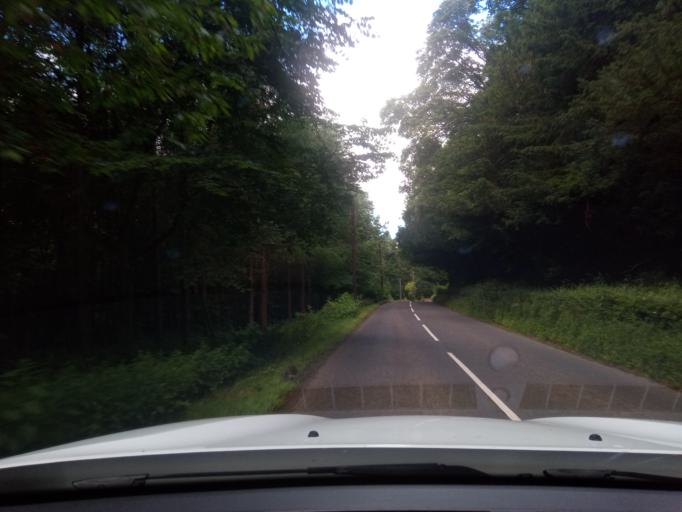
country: GB
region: Scotland
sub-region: The Scottish Borders
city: Selkirk
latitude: 55.5401
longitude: -2.8893
